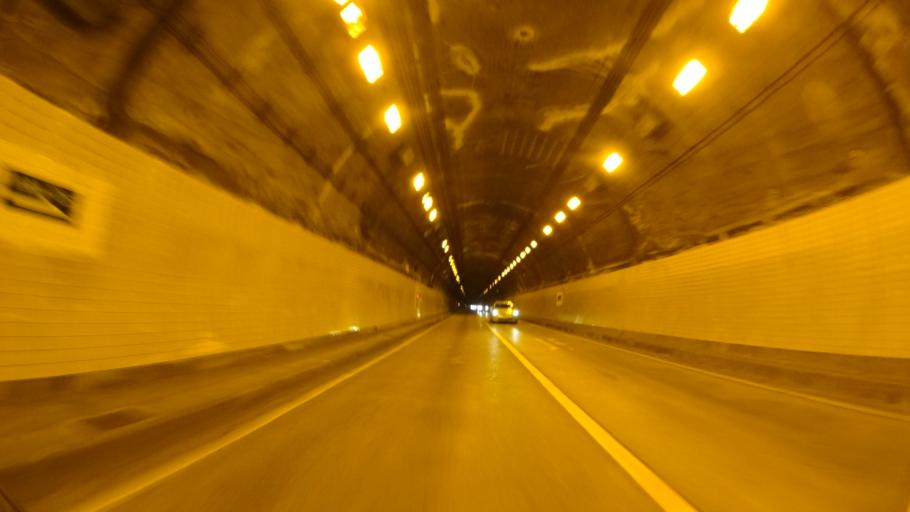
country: JP
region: Ehime
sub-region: Nishiuwa-gun
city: Ikata-cho
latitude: 33.4970
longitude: 132.3774
